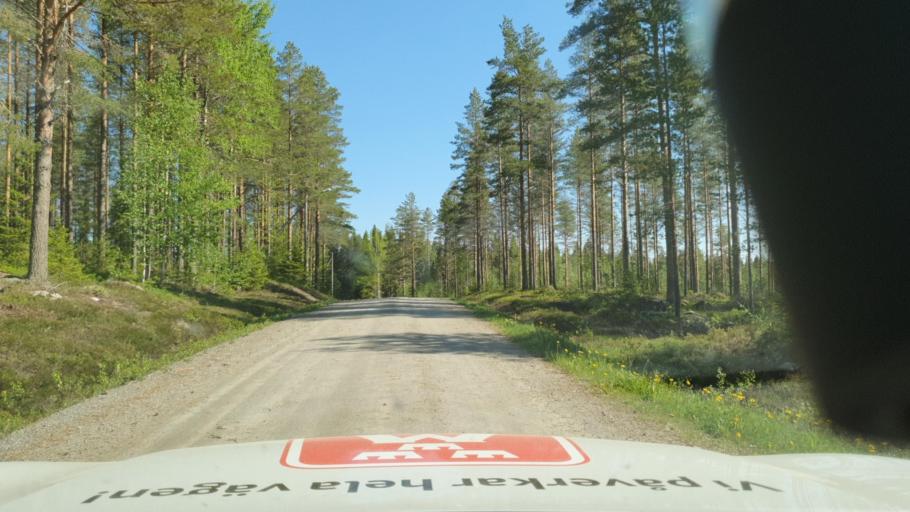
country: SE
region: Vaesterbotten
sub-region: Vannas Kommun
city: Vannasby
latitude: 63.9949
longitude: 19.7883
